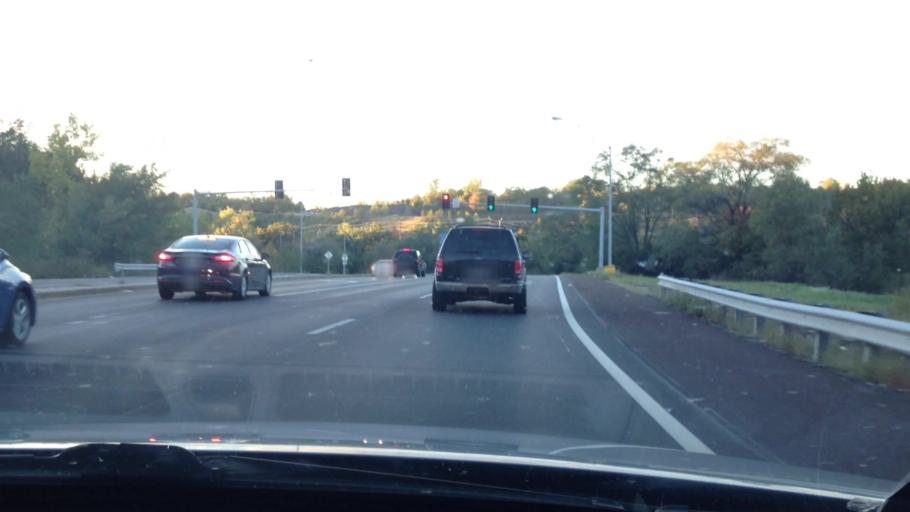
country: US
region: Missouri
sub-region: Jackson County
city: Raytown
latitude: 39.0117
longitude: -94.4984
